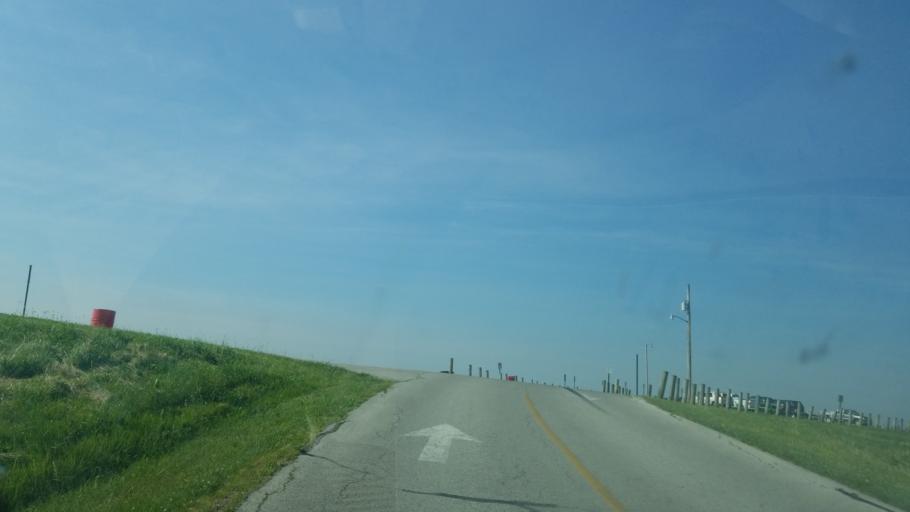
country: US
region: Ohio
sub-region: Hancock County
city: Findlay
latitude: 41.0212
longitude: -83.5806
